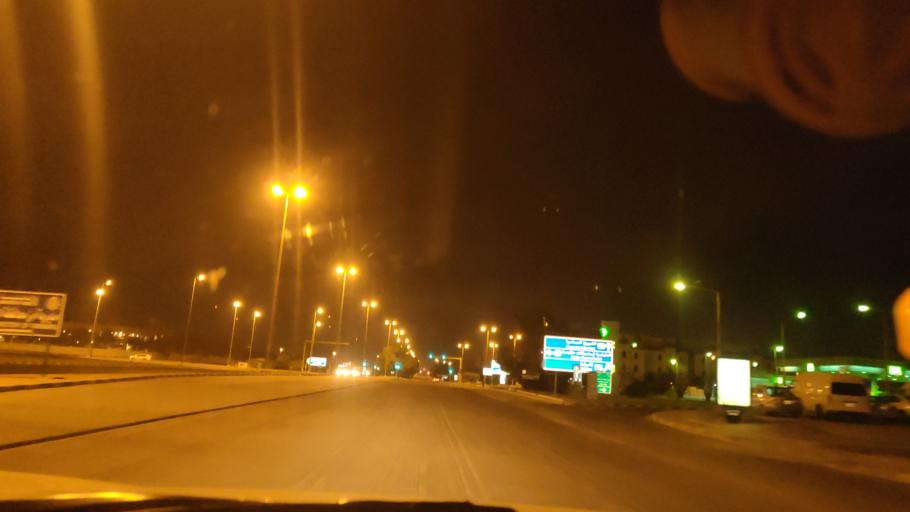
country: KW
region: Al Asimah
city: Ar Rabiyah
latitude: 29.2734
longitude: 47.9264
